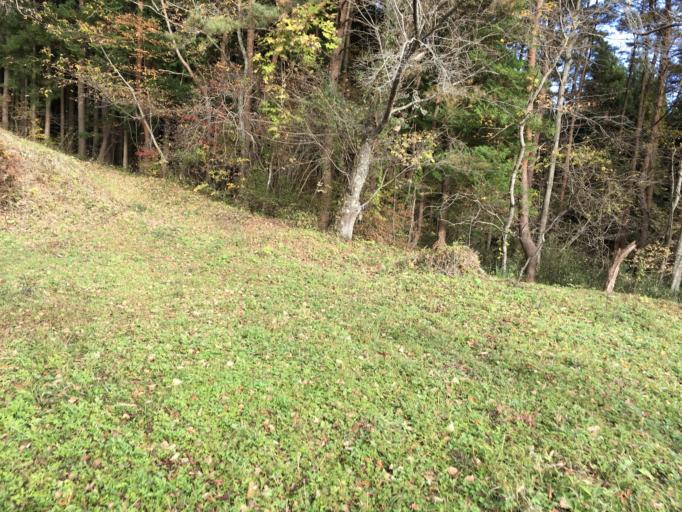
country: JP
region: Iwate
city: Ofunato
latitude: 38.9584
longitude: 141.4503
